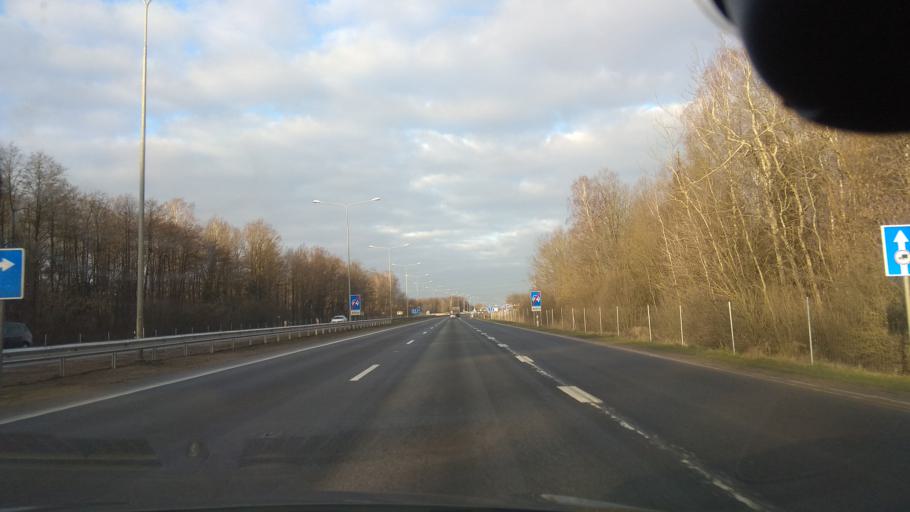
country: LT
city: Ramuciai
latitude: 54.9307
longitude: 24.0069
